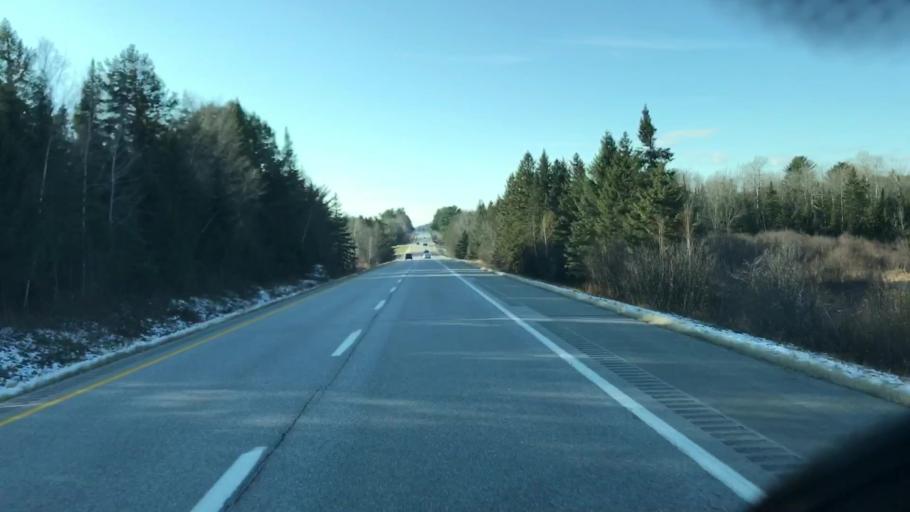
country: US
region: Maine
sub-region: Penobscot County
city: Carmel
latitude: 44.7817
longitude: -69.0815
